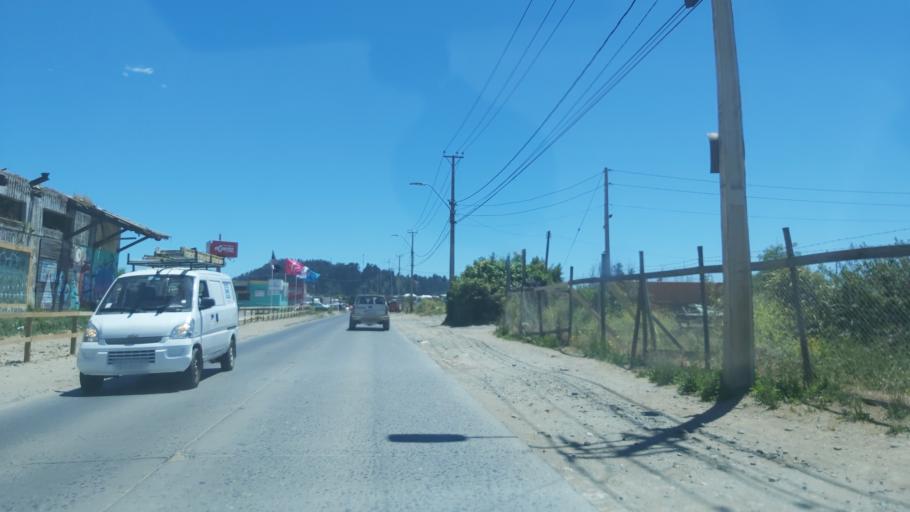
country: CL
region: Maule
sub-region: Provincia de Talca
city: Constitucion
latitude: -35.3369
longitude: -72.4032
